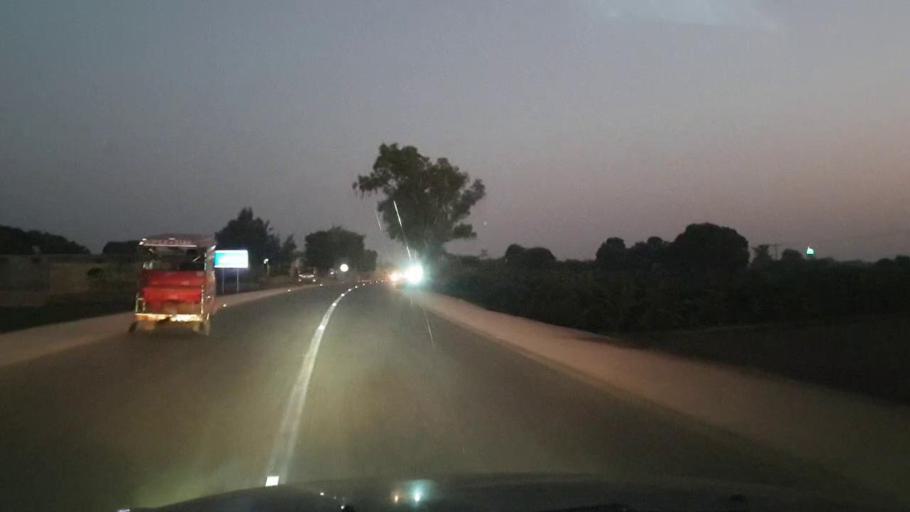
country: PK
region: Sindh
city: Chambar
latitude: 25.3805
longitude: 68.7768
